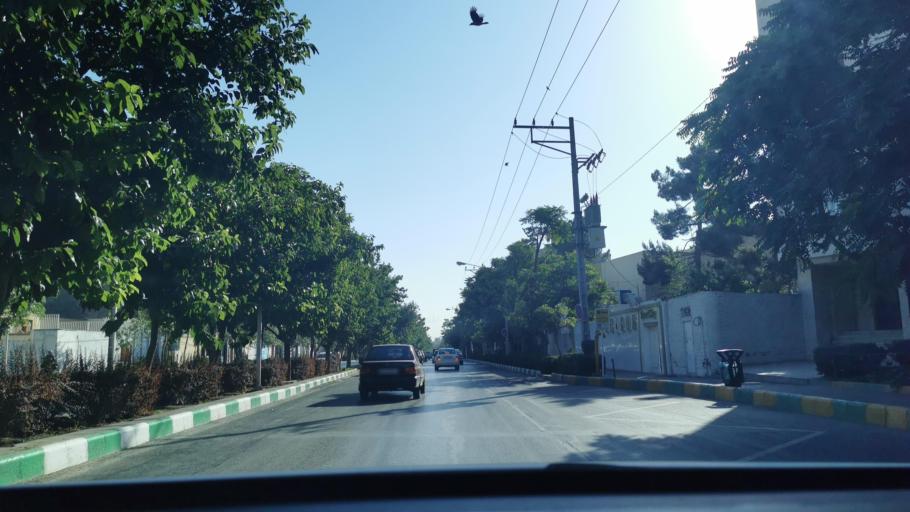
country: IR
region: Razavi Khorasan
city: Mashhad
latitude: 36.3152
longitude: 59.5187
